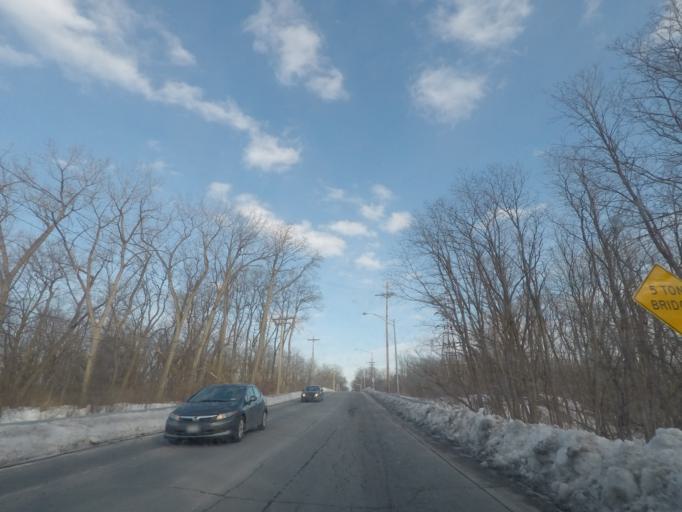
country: US
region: New York
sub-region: Schenectady County
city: Scotia
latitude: 42.8297
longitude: -73.9498
